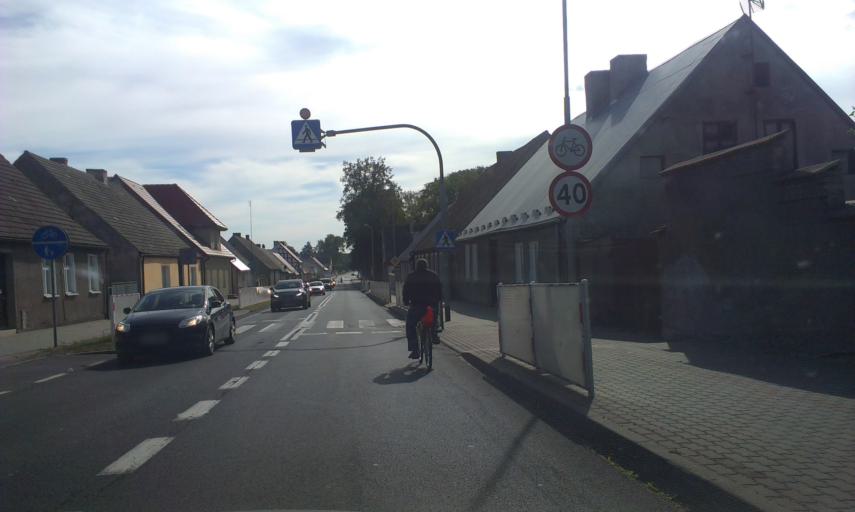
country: PL
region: Greater Poland Voivodeship
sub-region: Powiat zlotowski
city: Okonek
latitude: 53.5389
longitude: 16.8490
